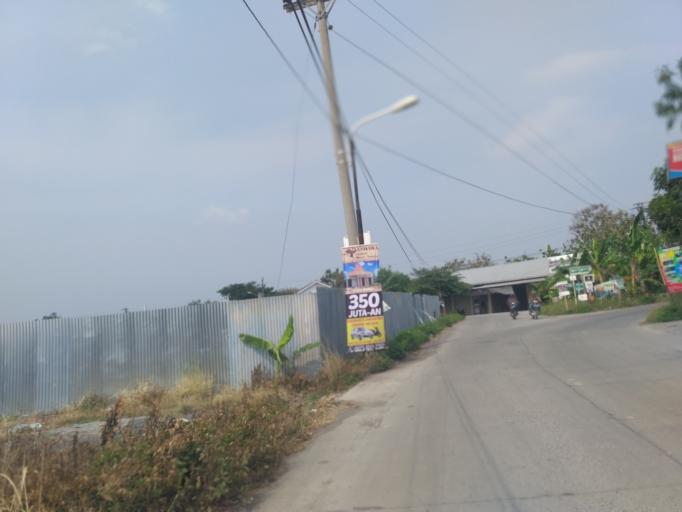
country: ID
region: Central Java
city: Mranggen
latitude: -7.0592
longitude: 110.4732
